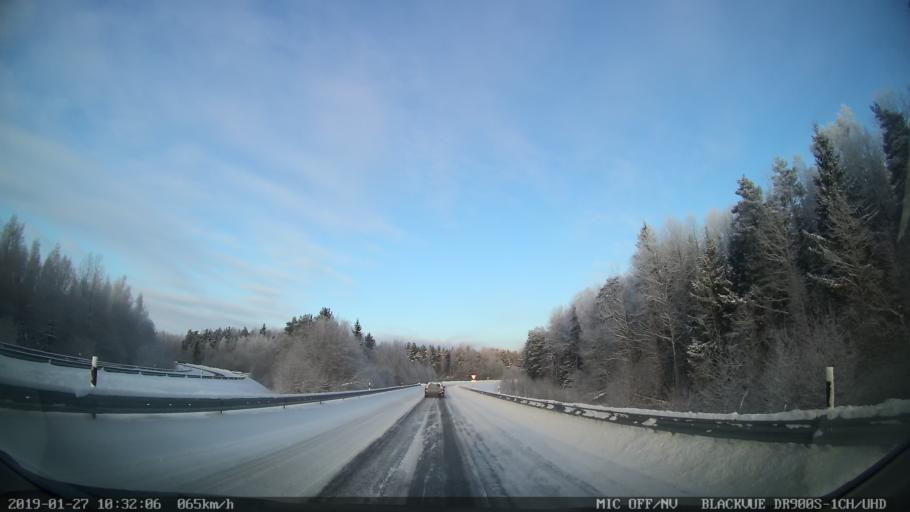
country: EE
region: Harju
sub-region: Raasiku vald
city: Raasiku
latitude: 59.4378
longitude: 25.1887
